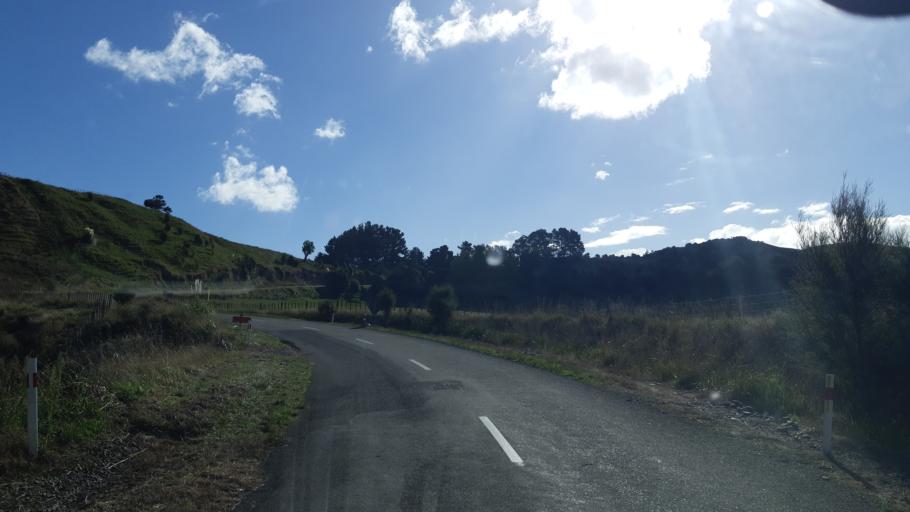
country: NZ
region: Manawatu-Wanganui
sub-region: Rangitikei District
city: Bulls
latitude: -39.9080
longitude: 175.3602
